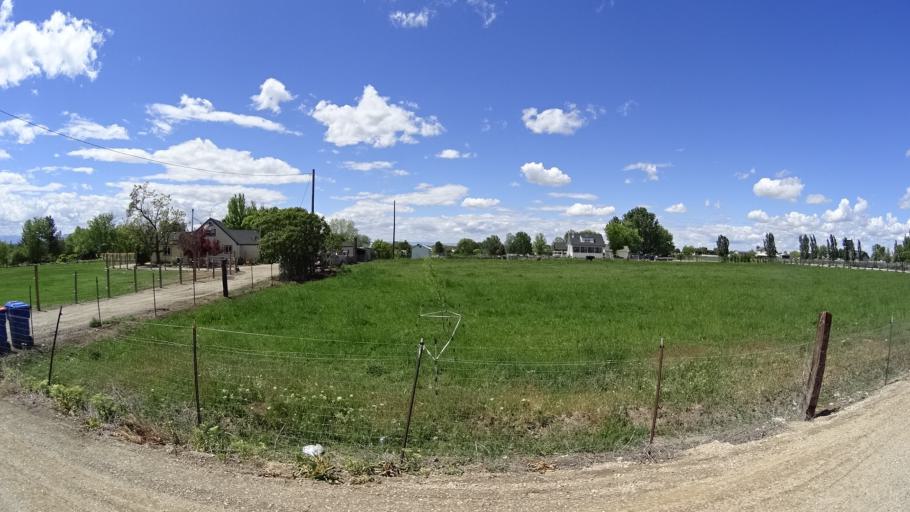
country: US
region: Idaho
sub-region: Ada County
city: Kuna
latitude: 43.5577
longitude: -116.4536
